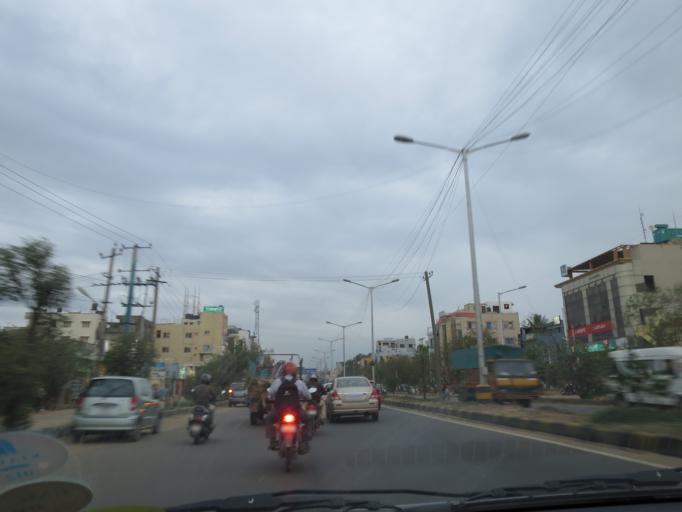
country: IN
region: Karnataka
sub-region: Bangalore Urban
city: Bangalore
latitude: 12.9626
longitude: 77.7018
